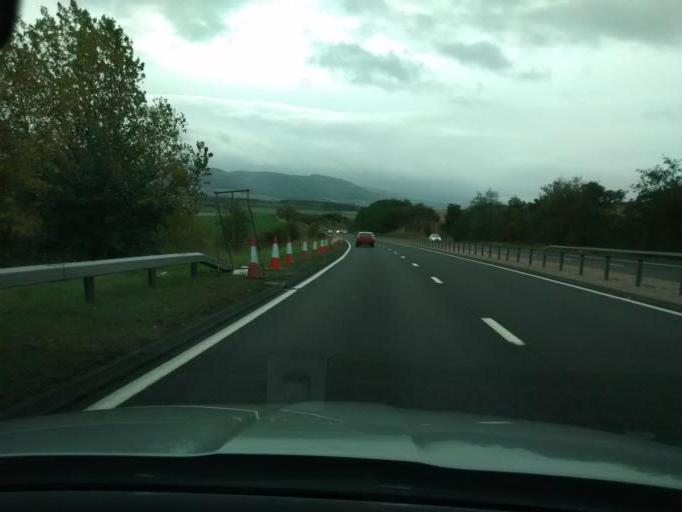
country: GB
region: Scotland
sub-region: Perth and Kinross
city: Methven
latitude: 56.3499
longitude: -3.5765
